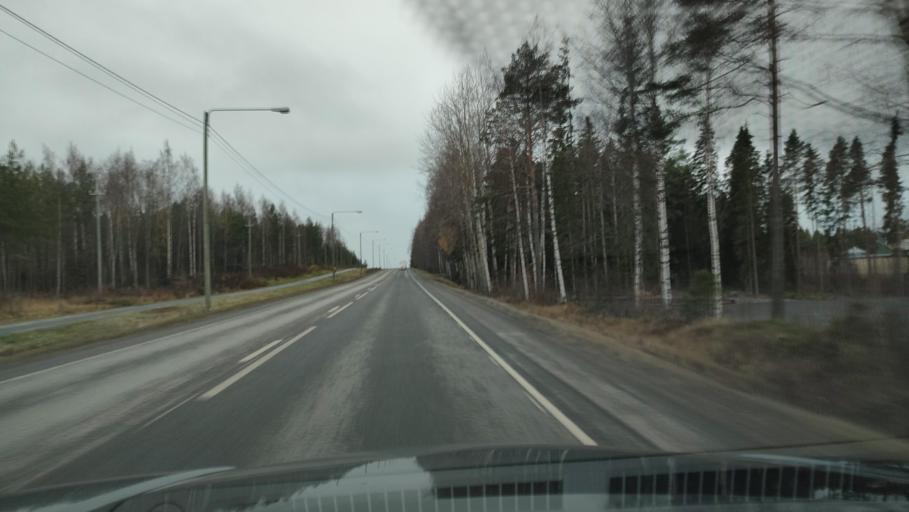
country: FI
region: Southern Ostrobothnia
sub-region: Seinaejoki
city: Seinaejoki
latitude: 62.7832
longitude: 22.7096
